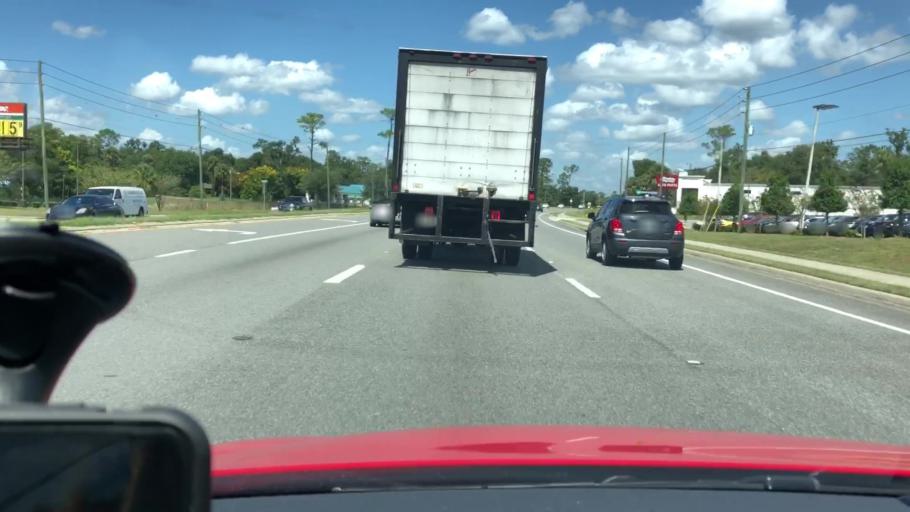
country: US
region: Florida
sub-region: Volusia County
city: De Land Southwest
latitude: 28.9906
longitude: -81.3015
